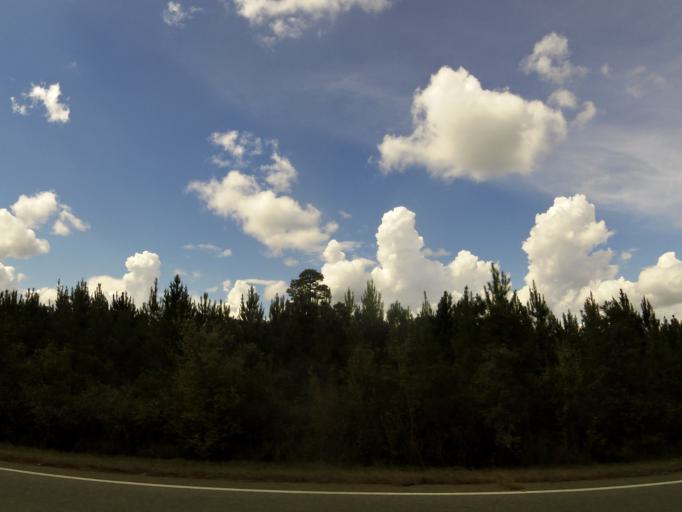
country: US
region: Georgia
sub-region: Brantley County
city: Nahunta
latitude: 31.0900
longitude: -82.0078
